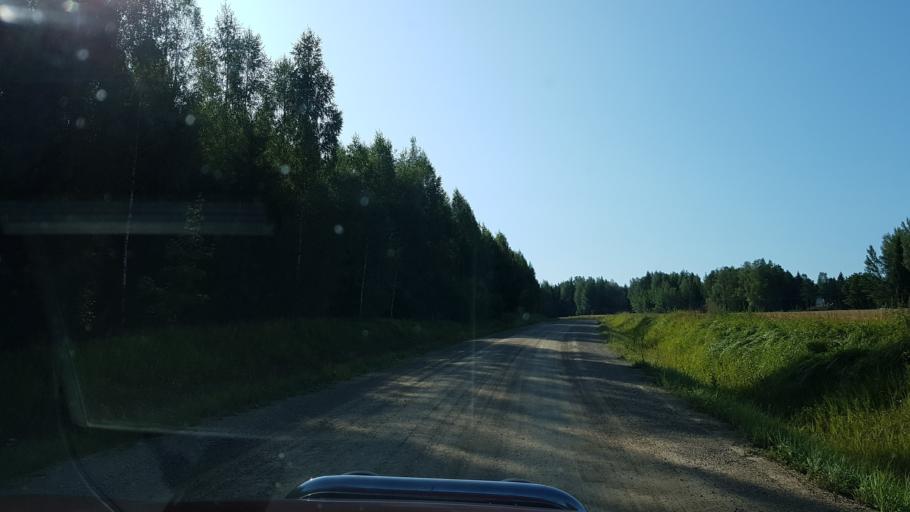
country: LV
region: Apes Novads
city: Ape
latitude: 57.6477
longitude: 26.7520
